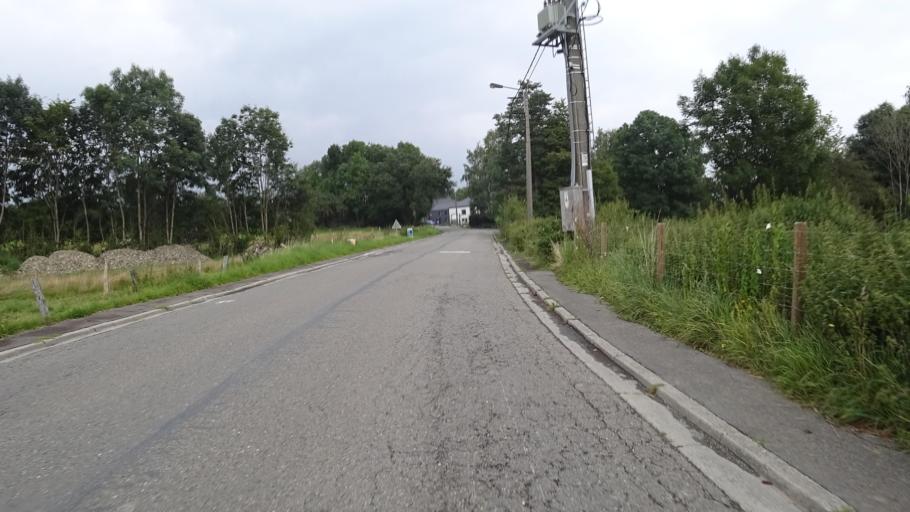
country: BE
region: Wallonia
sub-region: Province du Luxembourg
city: Chiny
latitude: 49.8092
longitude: 5.3280
